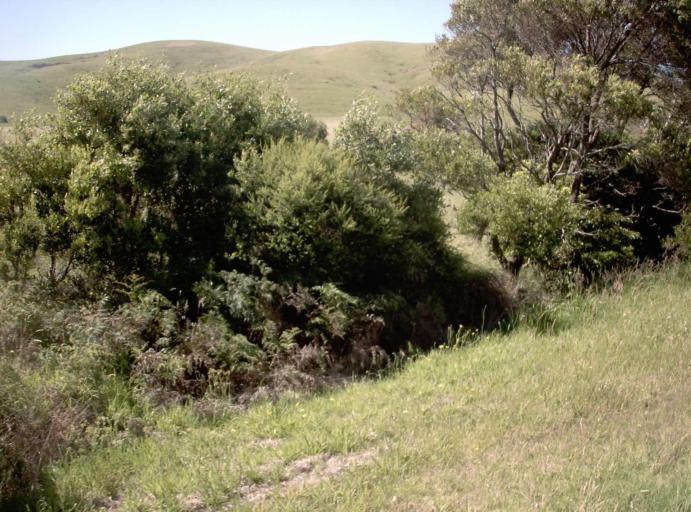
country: AU
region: Victoria
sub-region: Latrobe
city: Morwell
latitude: -38.6647
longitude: 146.4083
